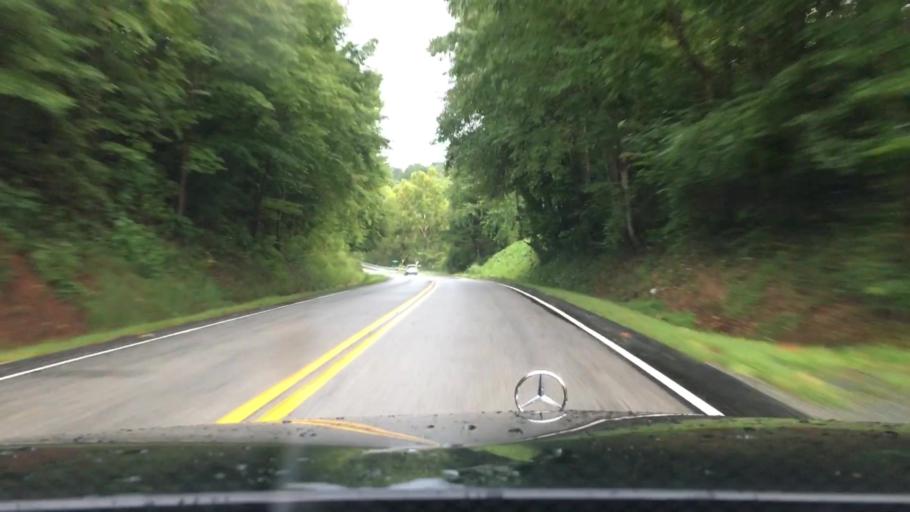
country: US
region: Virginia
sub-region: Amherst County
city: Amherst
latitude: 37.6948
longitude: -79.0293
